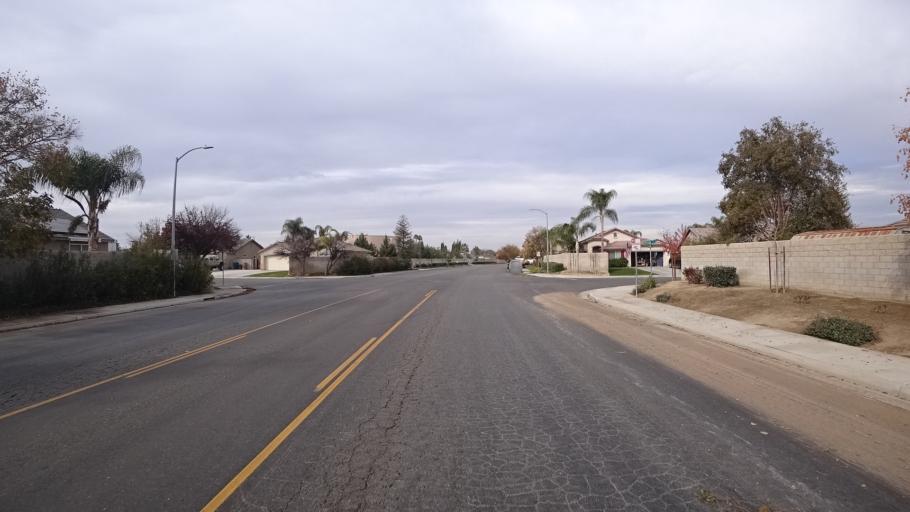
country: US
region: California
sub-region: Kern County
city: Rosedale
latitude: 35.3925
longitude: -119.1358
